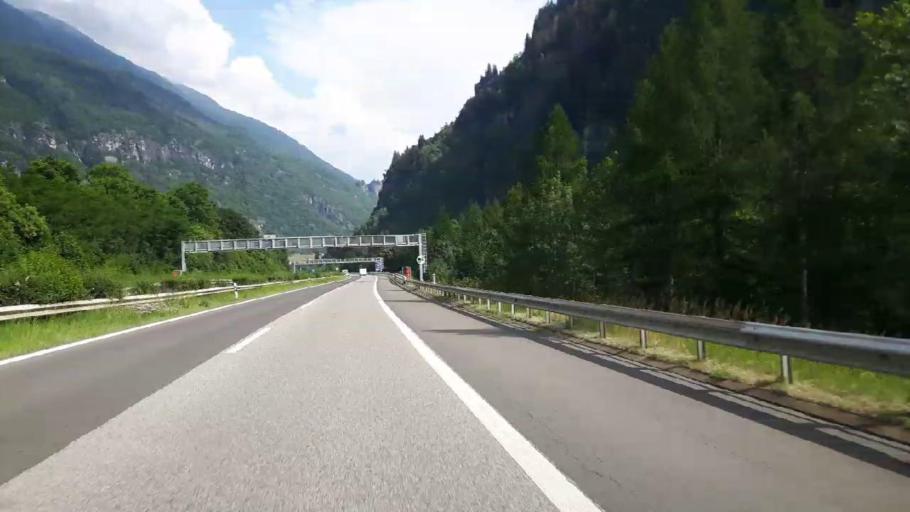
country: CH
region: Ticino
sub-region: Leventina District
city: Faido
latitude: 46.4715
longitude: 8.8100
